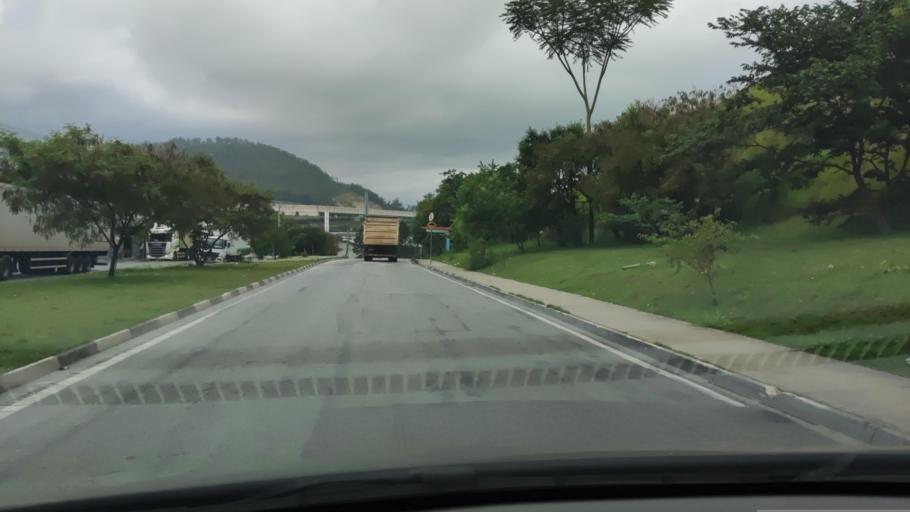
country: BR
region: Sao Paulo
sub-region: Cajamar
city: Cajamar
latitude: -23.3384
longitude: -46.8457
